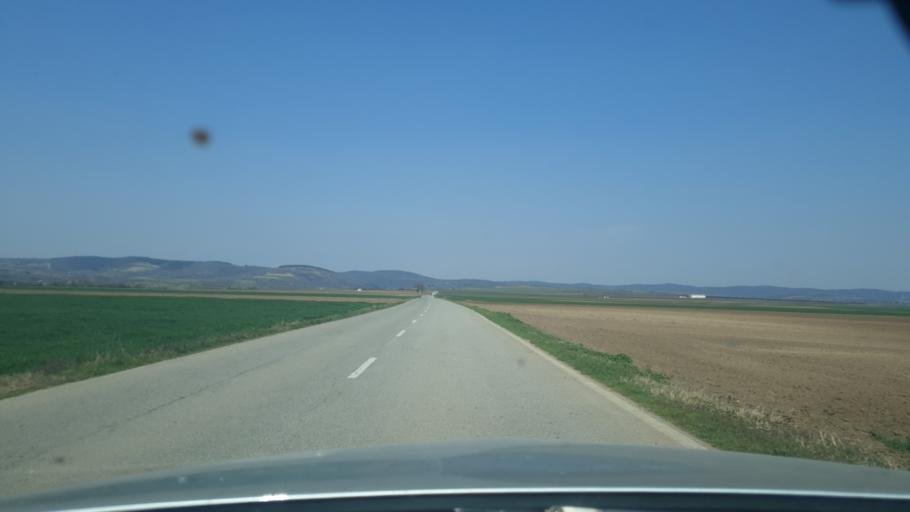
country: RS
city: Vrdnik
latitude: 45.0720
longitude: 19.7697
